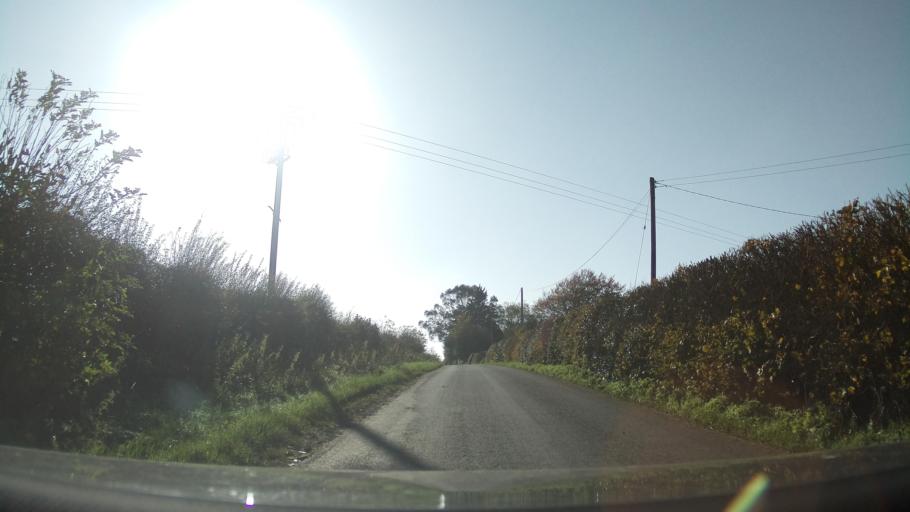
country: GB
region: England
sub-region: Somerset
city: Milborne Port
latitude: 51.0108
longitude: -2.5082
